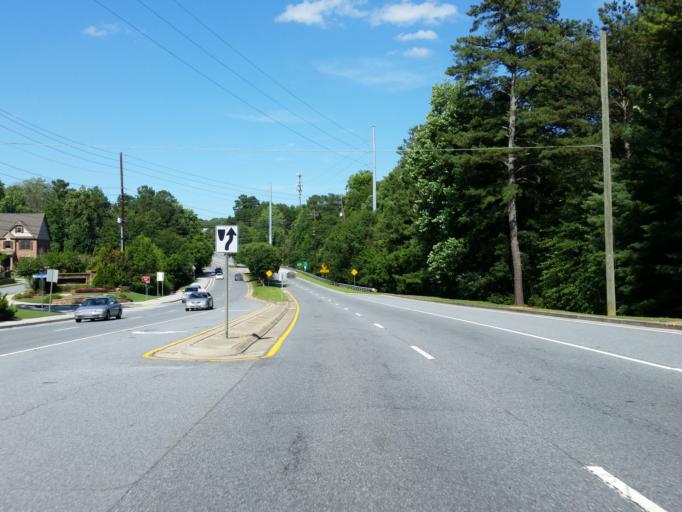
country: US
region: Georgia
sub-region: Fulton County
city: Roswell
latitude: 34.0020
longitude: -84.3967
